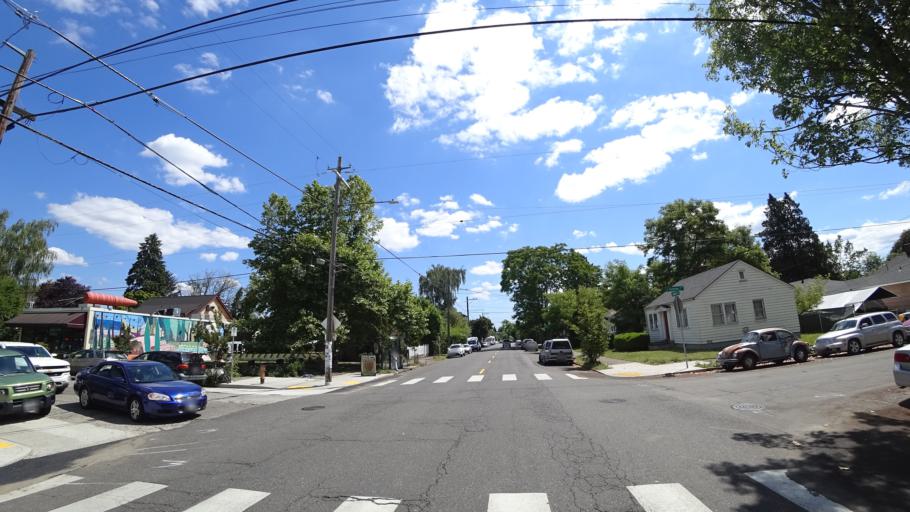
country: US
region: Oregon
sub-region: Multnomah County
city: Portland
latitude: 45.5605
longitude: -122.6750
